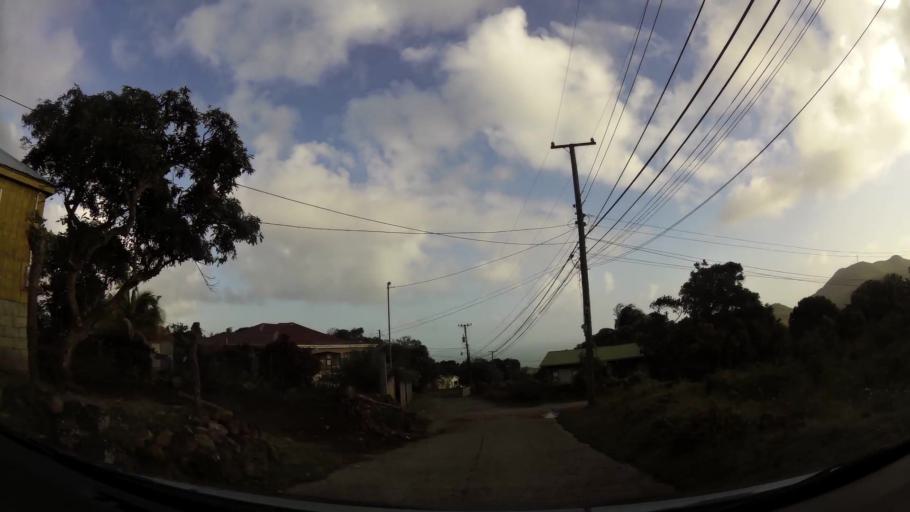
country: KN
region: Saint George Gingerland
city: Market Shop
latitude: 17.1372
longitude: -62.5745
